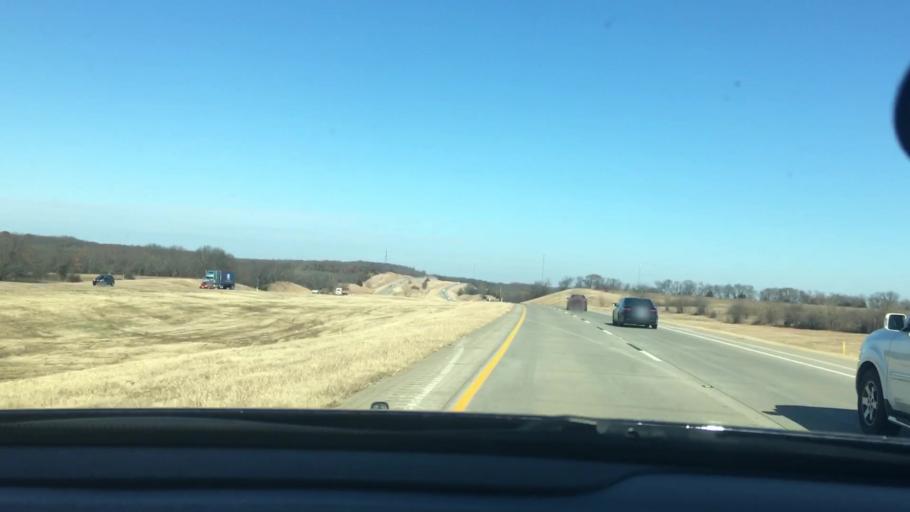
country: US
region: Oklahoma
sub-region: Love County
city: Marietta
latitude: 33.9795
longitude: -97.1346
